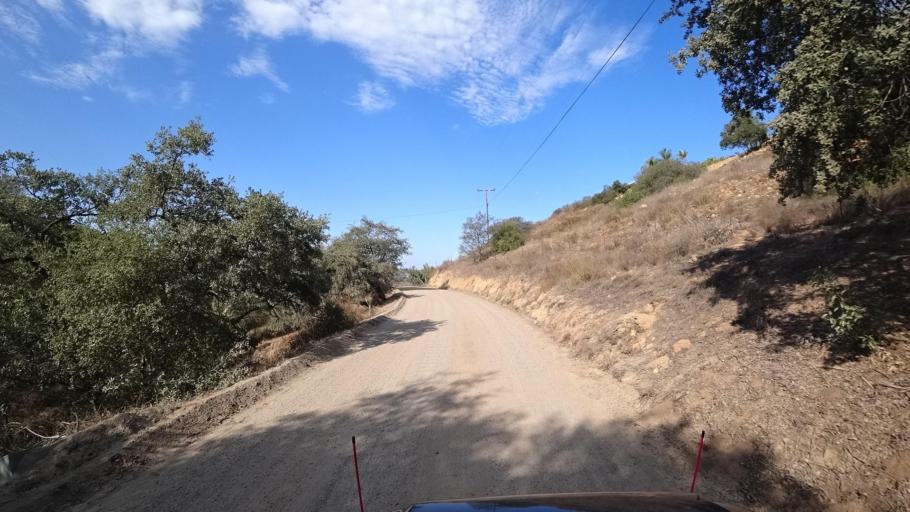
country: US
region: California
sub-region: San Diego County
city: San Pasqual
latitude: 33.1665
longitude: -116.9633
